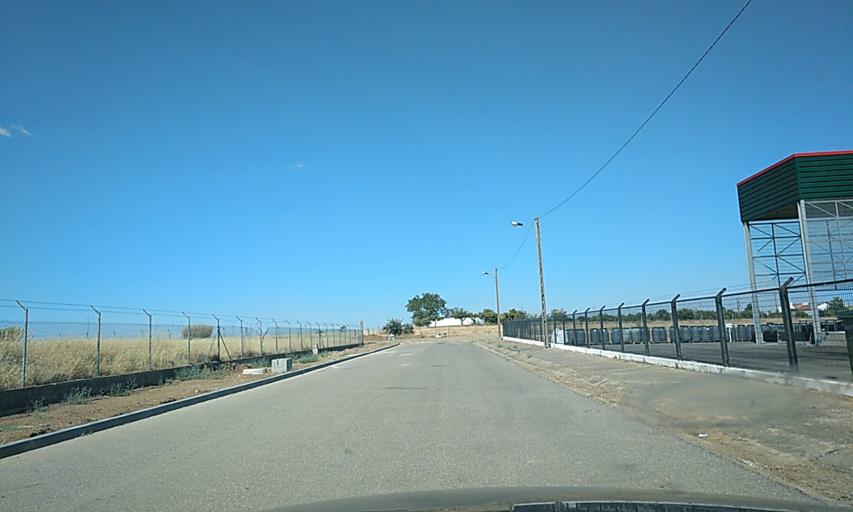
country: PT
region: Portalegre
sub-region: Campo Maior
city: Campo Maior
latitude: 39.0238
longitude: -7.0591
